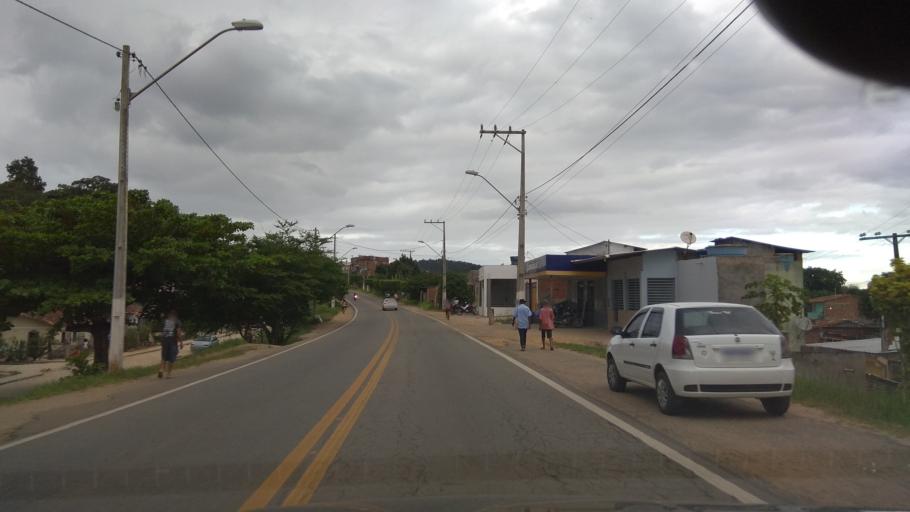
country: BR
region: Bahia
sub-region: Ubata
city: Ubata
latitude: -14.2103
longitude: -39.5240
